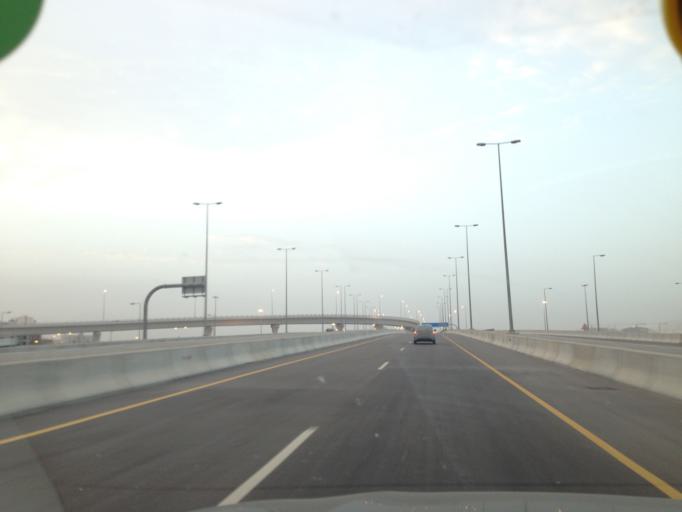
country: OM
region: Muhafazat Masqat
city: Bawshar
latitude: 23.5854
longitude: 58.3326
